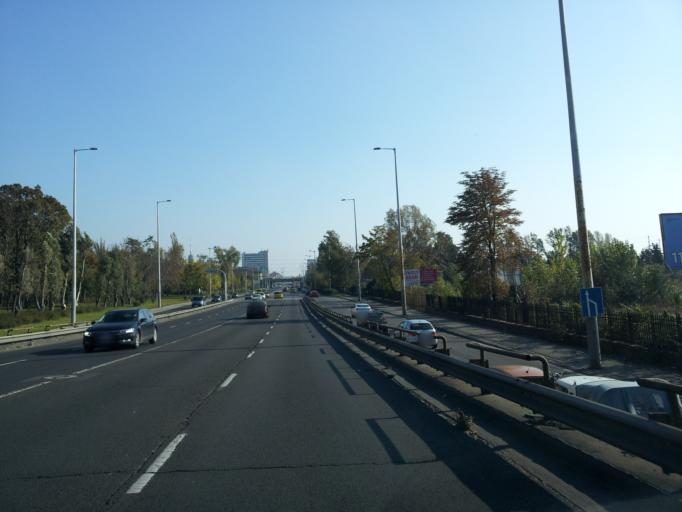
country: HU
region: Budapest
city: Budapest VIII. keruelet
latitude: 47.4746
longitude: 19.1012
